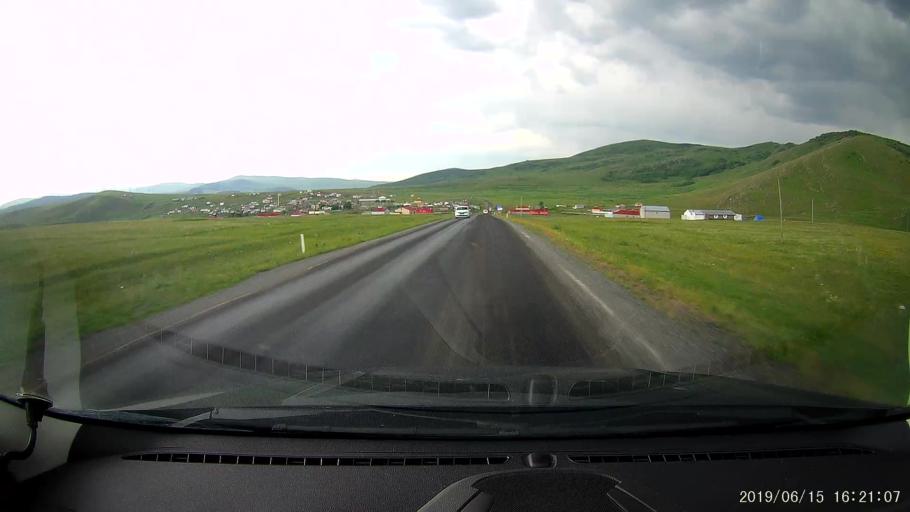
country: TR
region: Ardahan
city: Hanak
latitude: 41.2023
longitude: 42.8462
